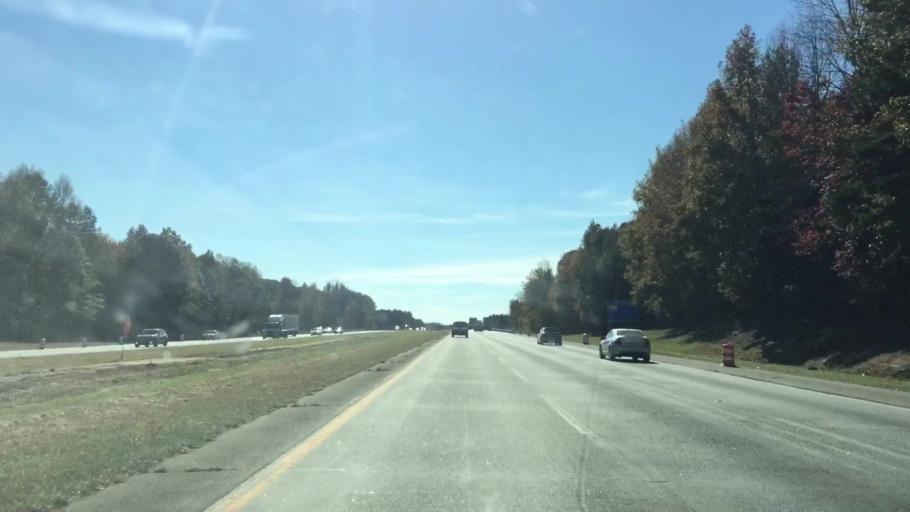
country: US
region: North Carolina
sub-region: Davidson County
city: Lexington
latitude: 35.8171
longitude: -80.1756
